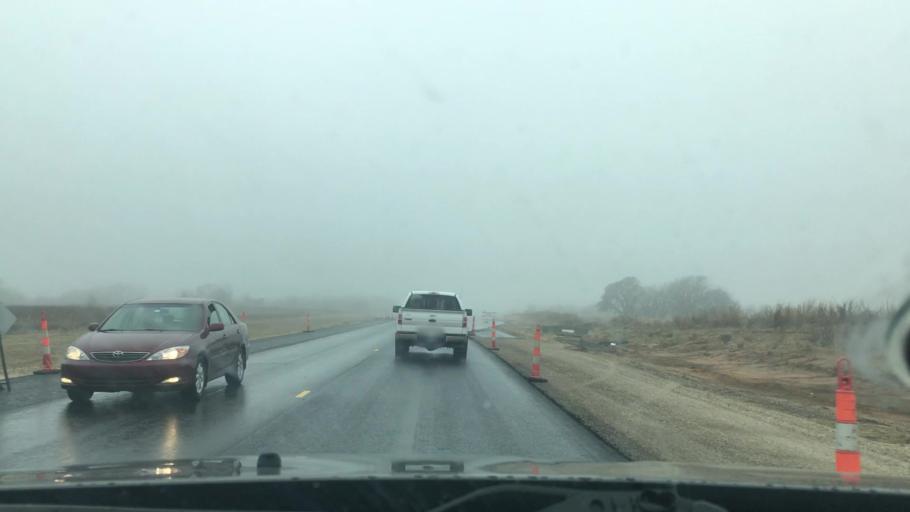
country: US
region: Oklahoma
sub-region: Johnston County
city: Tishomingo
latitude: 34.3260
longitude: -96.6622
